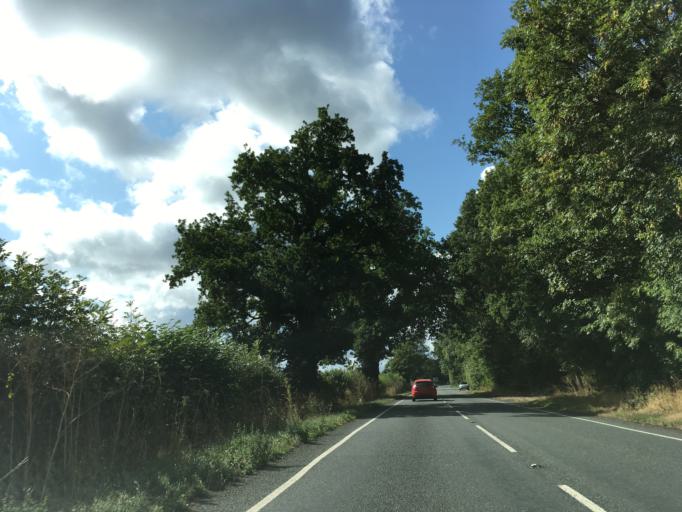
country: GB
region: England
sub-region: West Berkshire
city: Greenham
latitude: 51.3525
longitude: -1.3342
